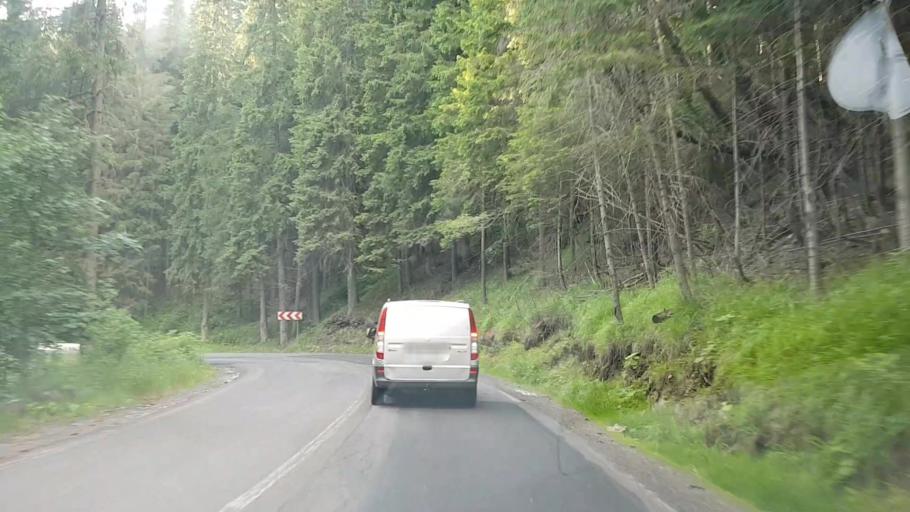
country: RO
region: Harghita
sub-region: Comuna Varsag
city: Varsag
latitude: 46.6659
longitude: 25.3065
